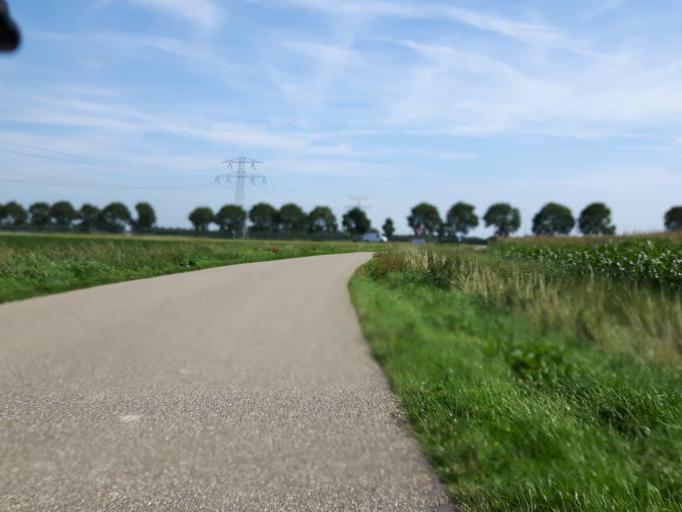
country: NL
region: Zeeland
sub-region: Gemeente Goes
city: Goes
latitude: 51.4766
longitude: 3.8873
